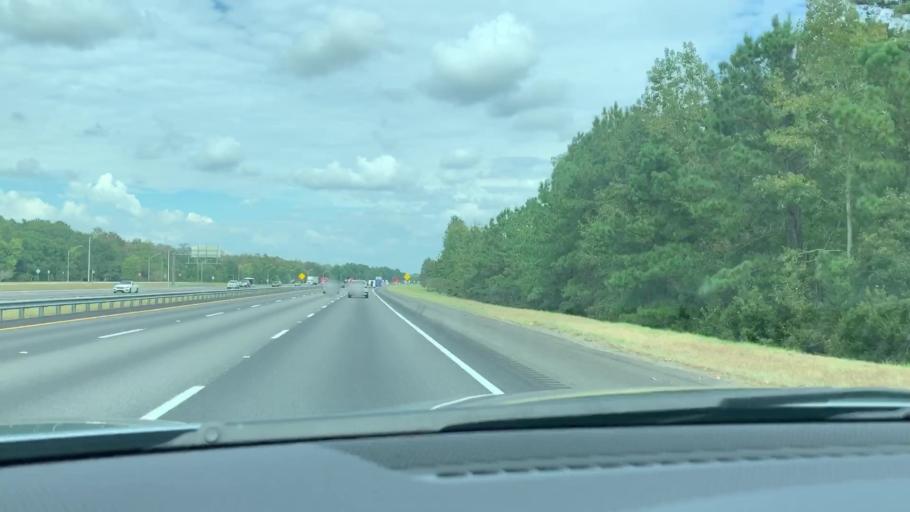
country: US
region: Georgia
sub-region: Chatham County
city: Port Wentworth
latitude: 32.2186
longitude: -81.1714
